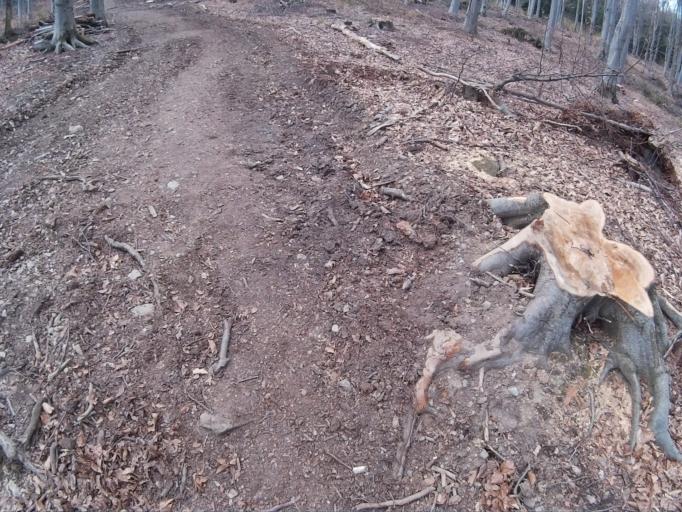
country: AT
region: Burgenland
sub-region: Politischer Bezirk Oberwart
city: Rechnitz
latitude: 47.3526
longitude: 16.4376
